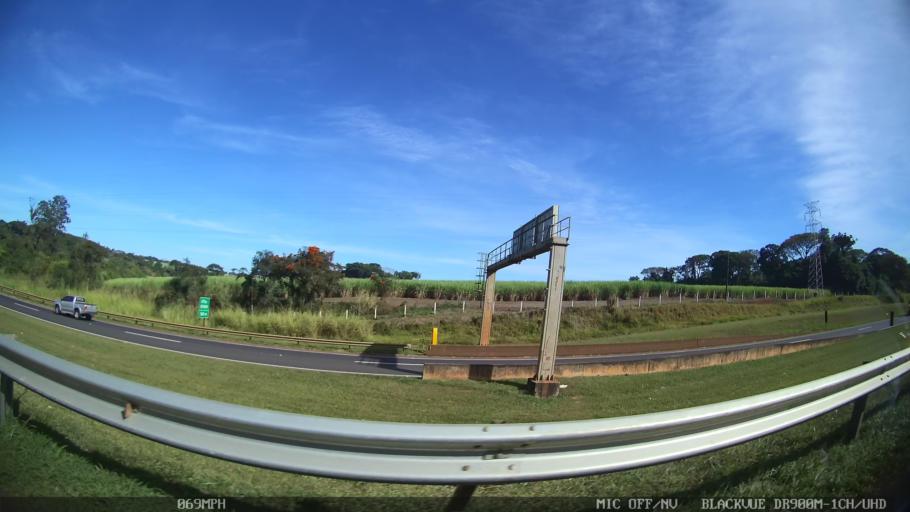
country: BR
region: Sao Paulo
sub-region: Araras
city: Araras
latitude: -22.3066
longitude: -47.3916
